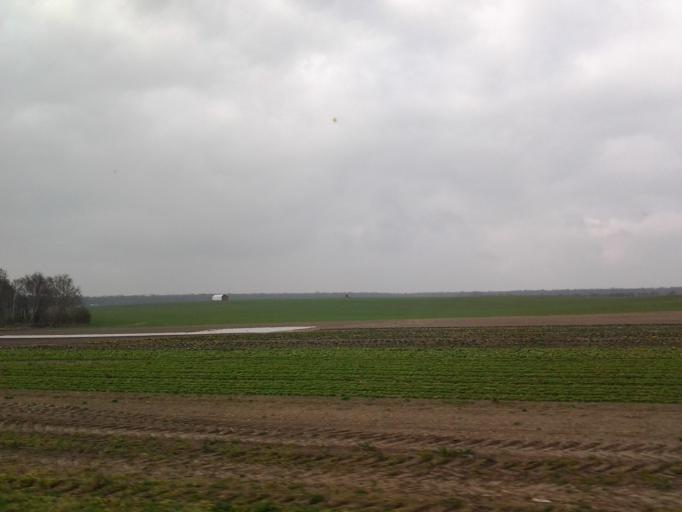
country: DE
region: Berlin
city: Staaken
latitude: 52.5055
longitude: 13.1222
